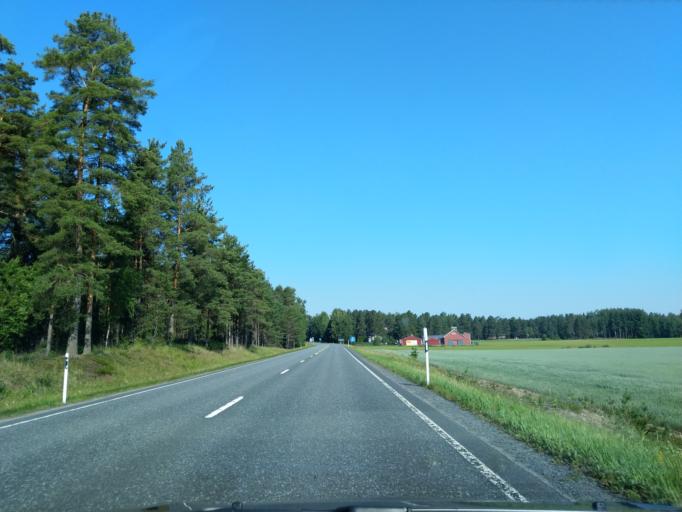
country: FI
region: Haeme
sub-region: Forssa
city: Humppila
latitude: 60.9598
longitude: 23.3255
